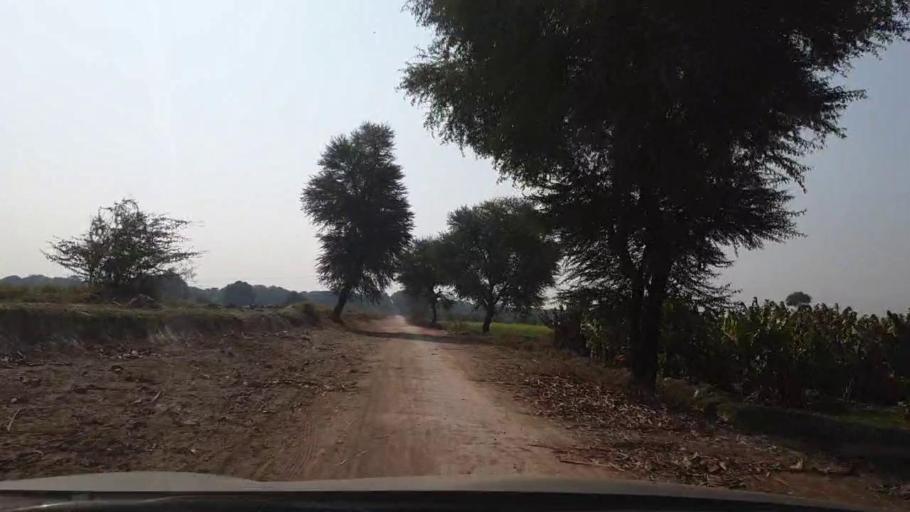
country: PK
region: Sindh
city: Tando Allahyar
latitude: 25.5010
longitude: 68.7860
